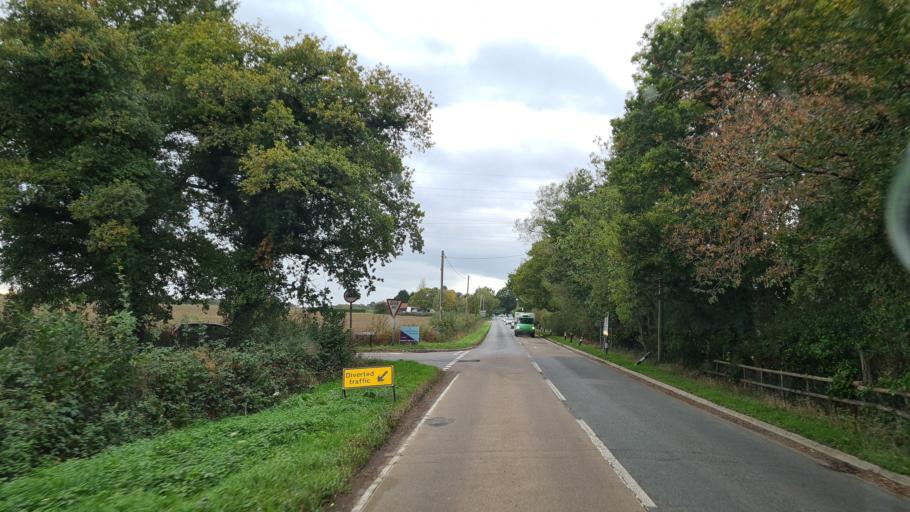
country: GB
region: England
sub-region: West Sussex
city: Bewbush
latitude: 51.0381
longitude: -0.2443
